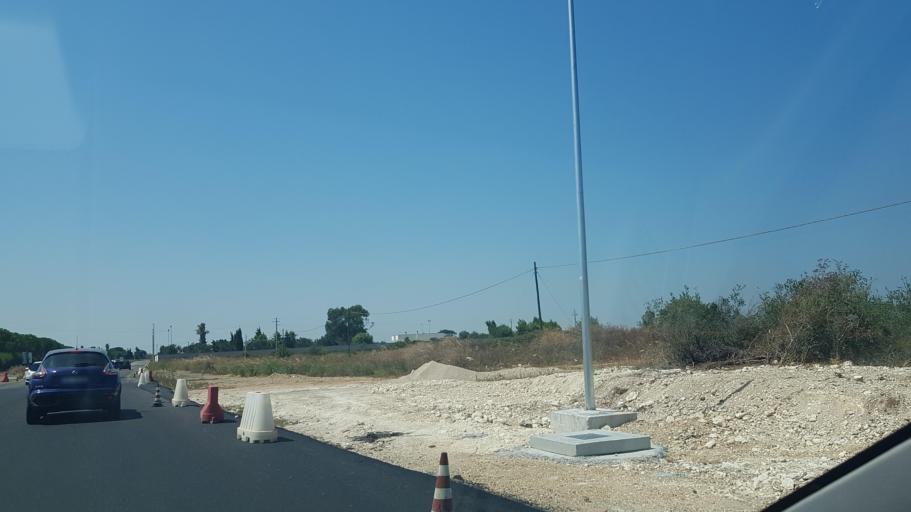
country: IT
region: Apulia
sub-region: Provincia di Lecce
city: Merine
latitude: 40.3353
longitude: 18.2356
